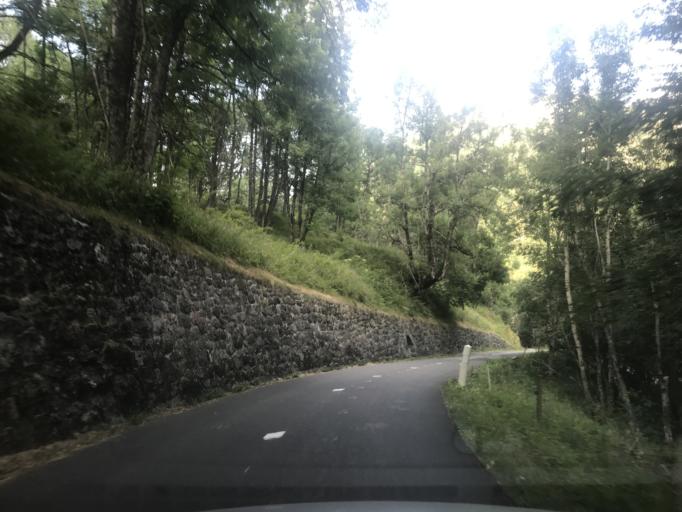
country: FR
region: Rhone-Alpes
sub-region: Departement de la Savoie
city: Saint-Etienne-de-Cuines
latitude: 45.2758
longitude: 6.2056
